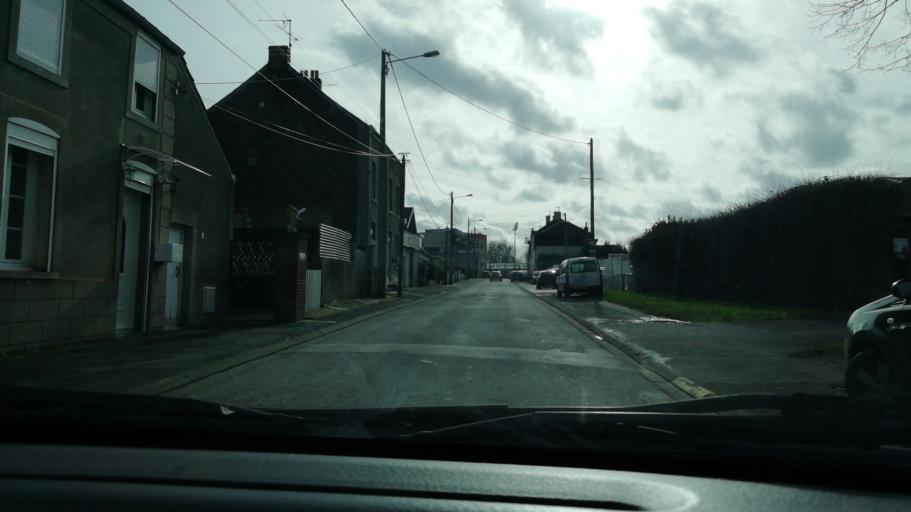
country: FR
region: Nord-Pas-de-Calais
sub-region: Departement du Nord
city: Louvroil
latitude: 50.2797
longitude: 3.9538
